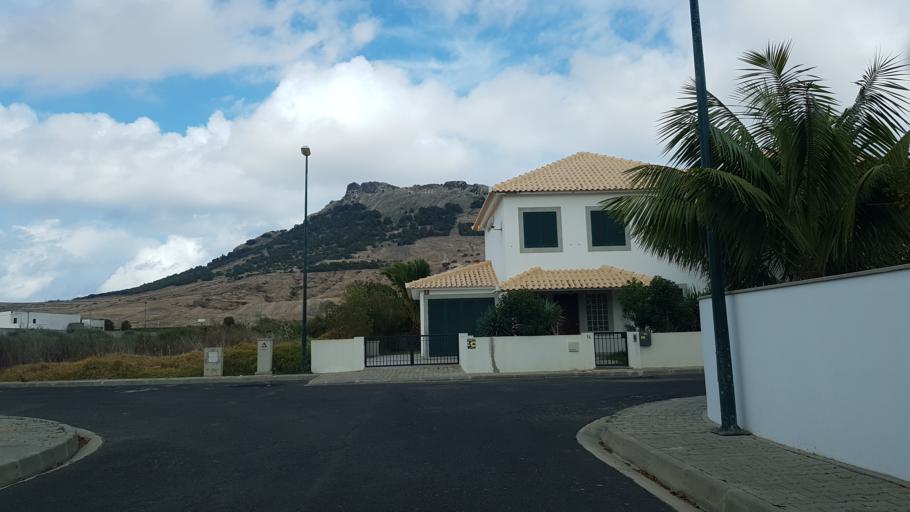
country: PT
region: Madeira
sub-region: Porto Santo
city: Vila de Porto Santo
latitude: 33.0453
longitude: -16.3576
